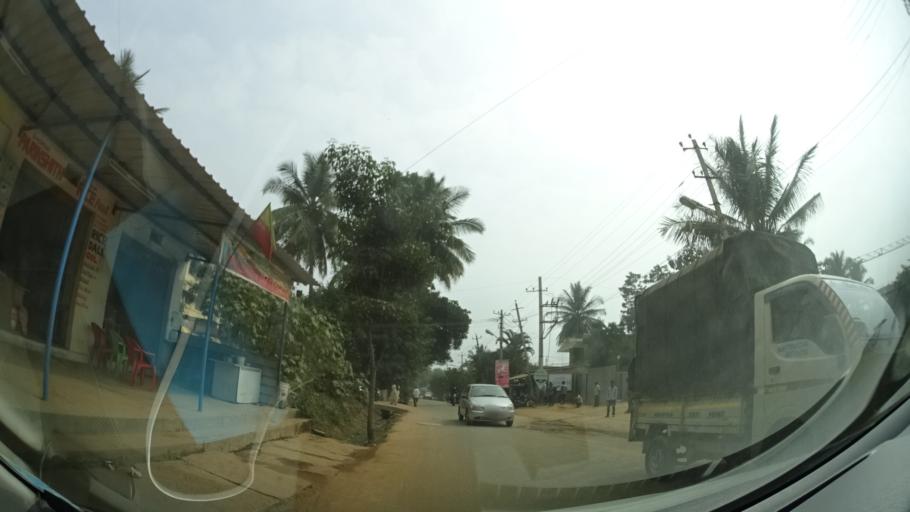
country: IN
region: Karnataka
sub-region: Bangalore Rural
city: Hoskote
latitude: 12.9649
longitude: 77.7574
